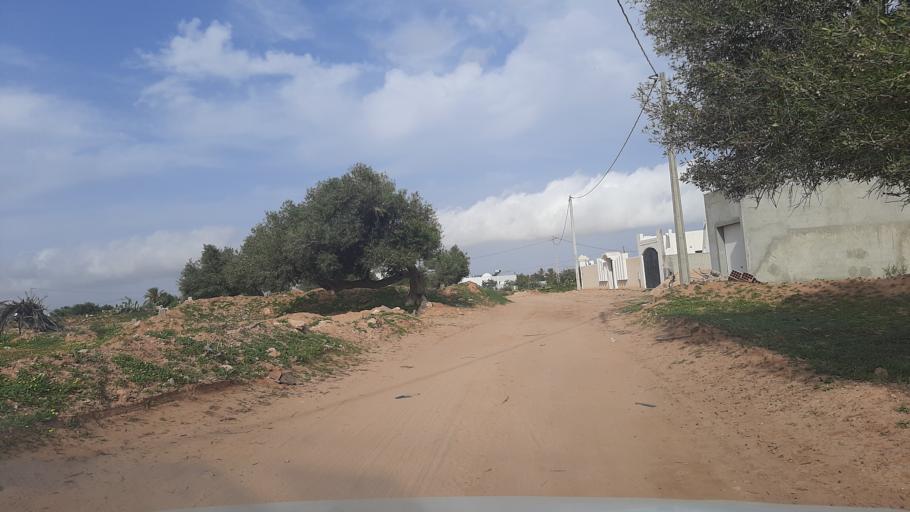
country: TN
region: Madanin
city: Midoun
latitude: 33.8045
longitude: 11.0253
